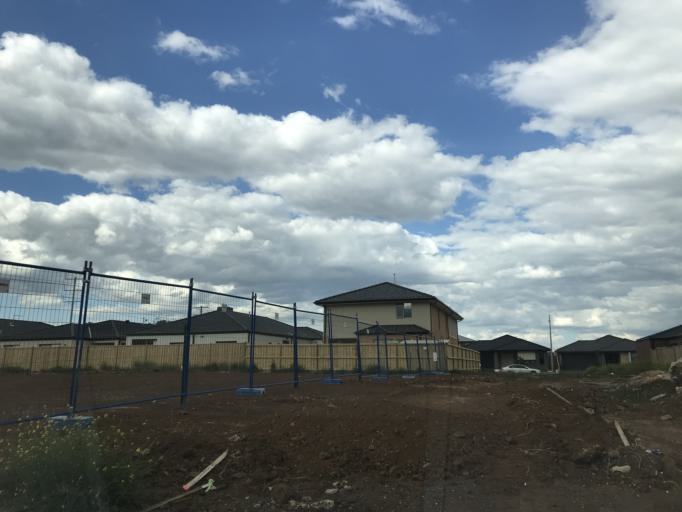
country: AU
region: Victoria
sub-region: Wyndham
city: Truganina
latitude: -37.8240
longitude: 144.7267
